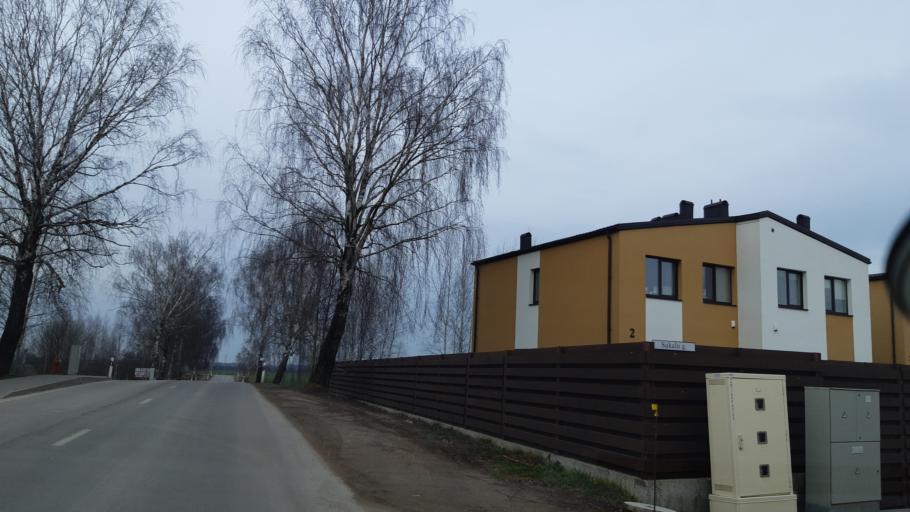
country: LT
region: Kauno apskritis
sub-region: Kauno rajonas
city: Akademija (Kaunas)
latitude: 54.9491
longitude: 23.8285
